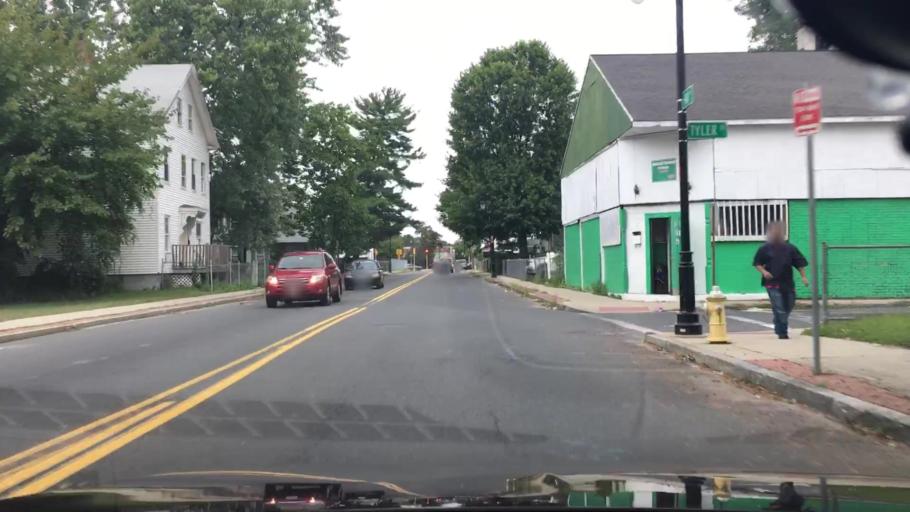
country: US
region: Massachusetts
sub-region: Hampden County
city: Springfield
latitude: 42.1059
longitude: -72.5735
